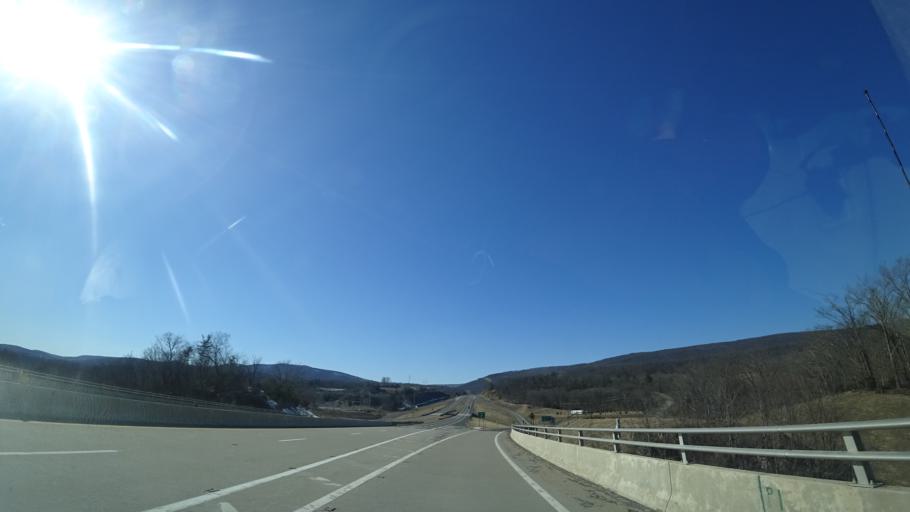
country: US
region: West Virginia
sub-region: Hardy County
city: Moorefield
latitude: 39.0451
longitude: -78.7352
